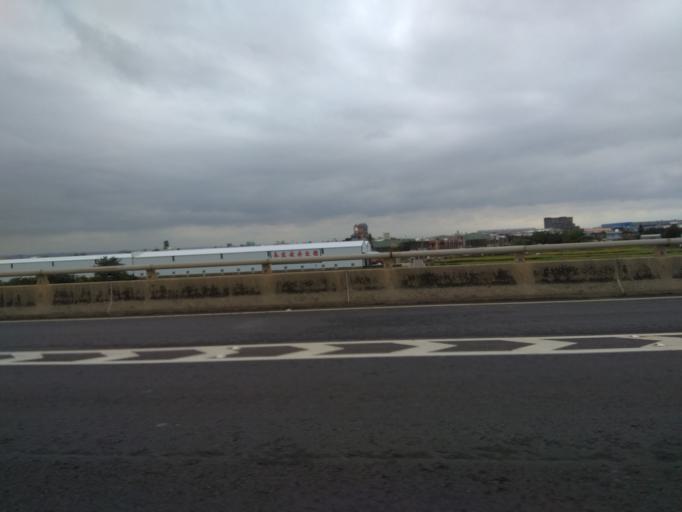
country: TW
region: Taiwan
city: Taoyuan City
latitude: 25.0876
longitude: 121.1863
